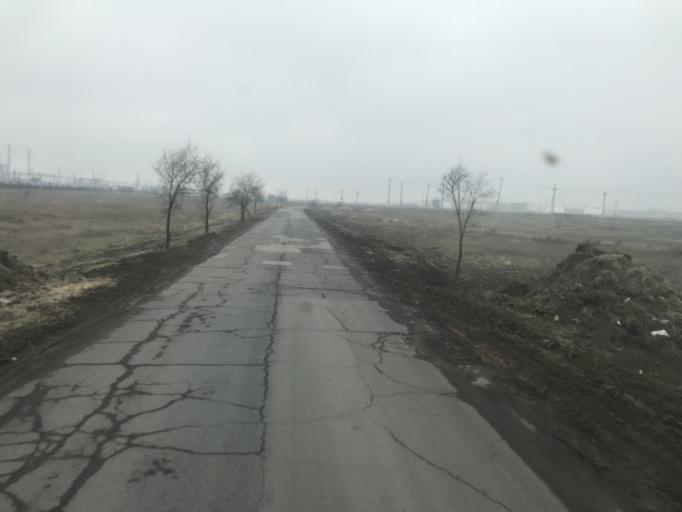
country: RU
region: Volgograd
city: Svetlyy Yar
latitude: 48.4914
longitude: 44.6591
